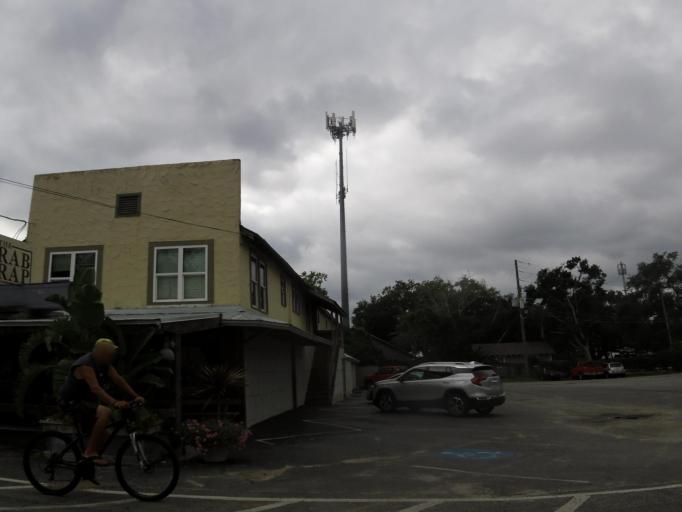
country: US
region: Georgia
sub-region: Glynn County
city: Saint Simons Island
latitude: 31.1407
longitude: -81.3814
